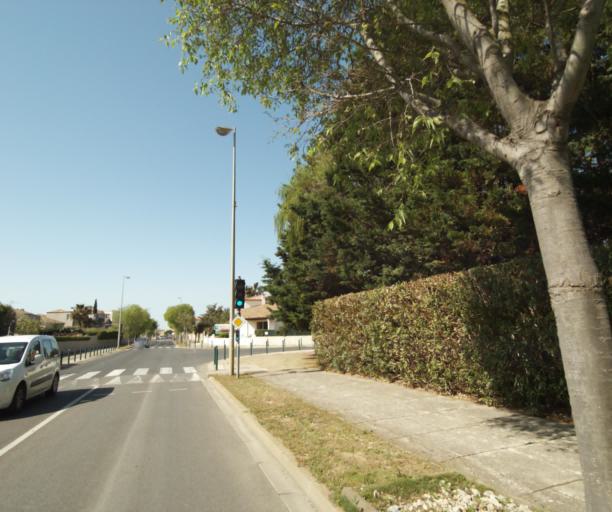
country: FR
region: Languedoc-Roussillon
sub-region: Departement de l'Herault
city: Lattes
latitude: 43.5733
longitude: 3.9086
